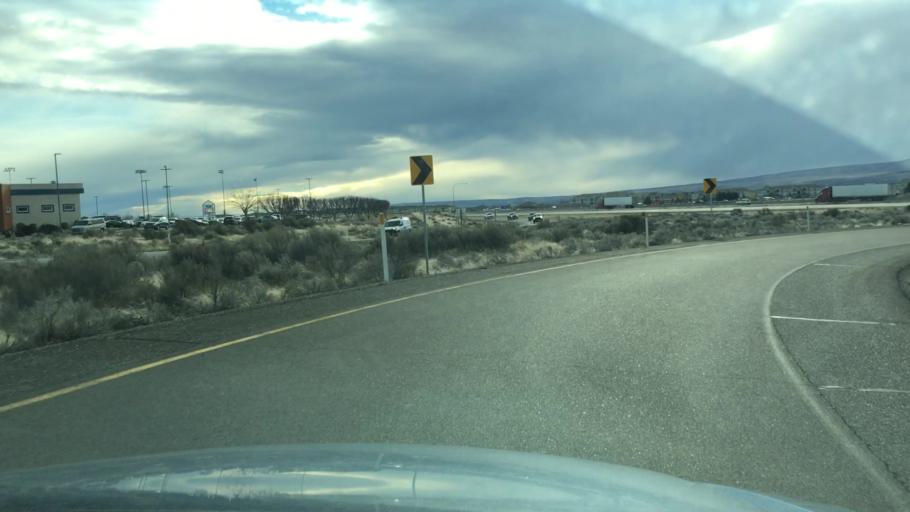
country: US
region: Washington
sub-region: Franklin County
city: West Pasco
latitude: 46.2668
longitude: -119.1806
